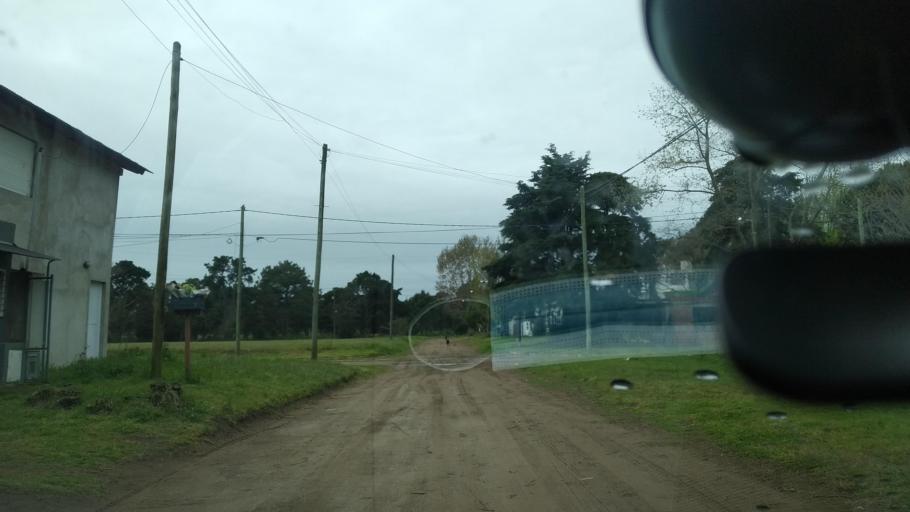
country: AR
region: Buenos Aires
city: Mar del Tuyu
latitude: -36.5299
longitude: -56.7135
